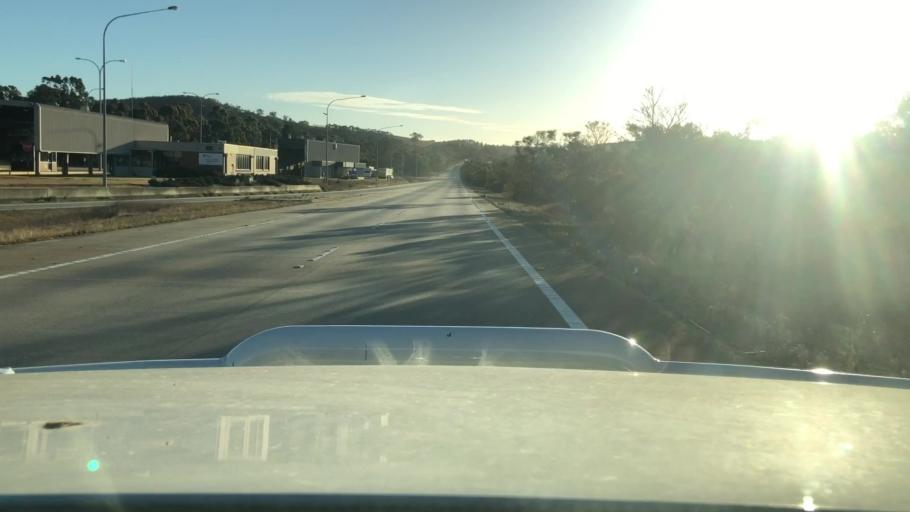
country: AU
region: New South Wales
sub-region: Wingecarribee
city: Bundanoon
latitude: -34.7049
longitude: 150.0144
